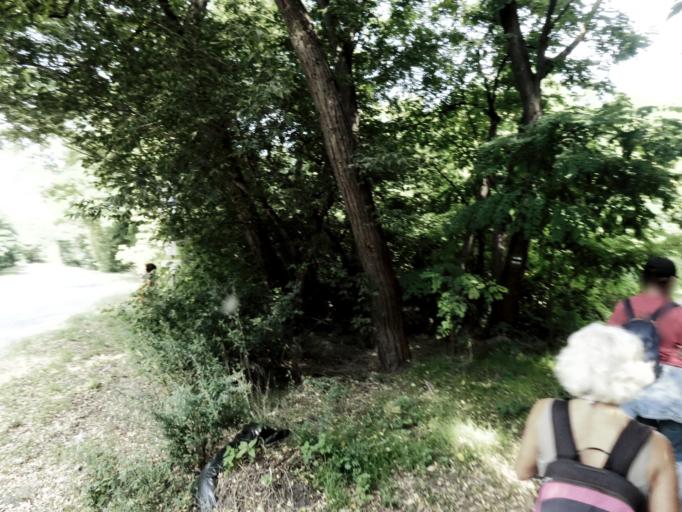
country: HU
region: Pest
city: Danszentmiklos
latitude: 47.1626
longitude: 19.5051
